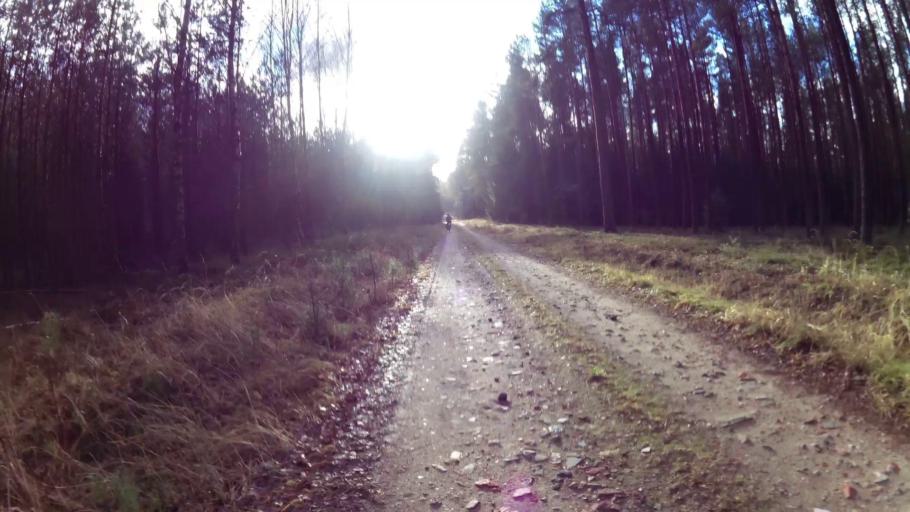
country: PL
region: West Pomeranian Voivodeship
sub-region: Powiat koszalinski
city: Sianow
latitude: 54.0867
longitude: 16.2924
